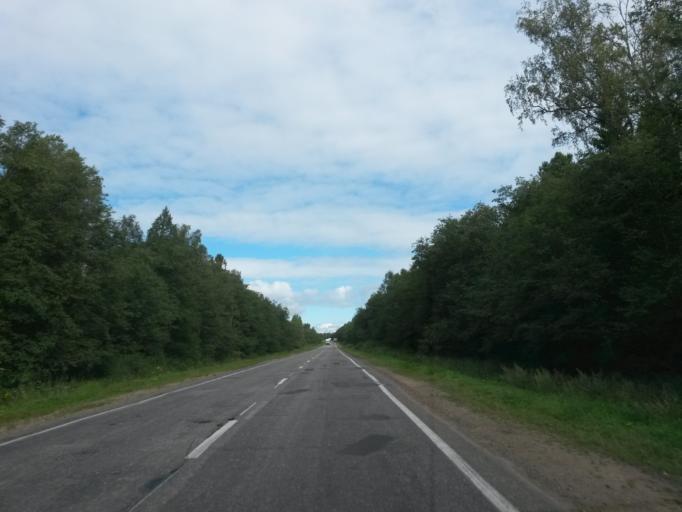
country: RU
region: Jaroslavl
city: Gavrilov-Yam
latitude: 57.4340
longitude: 39.9180
